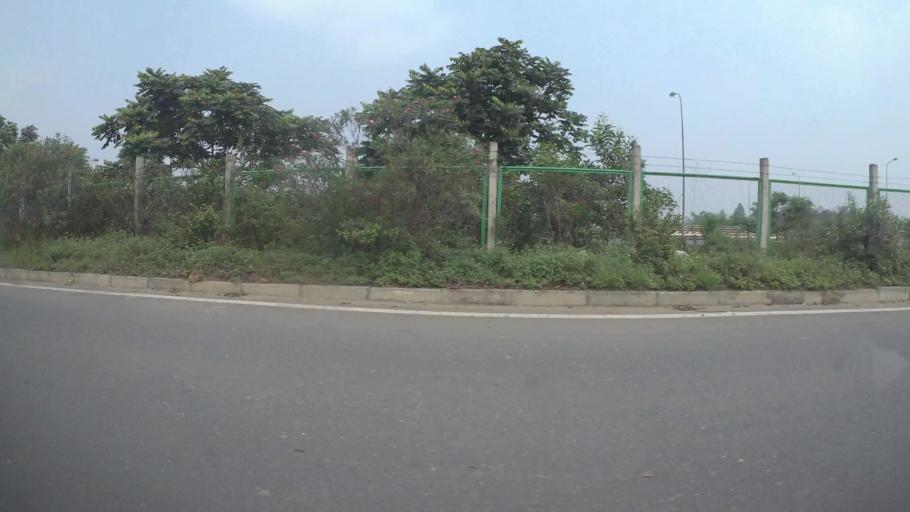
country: VN
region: Ha Noi
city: Quoc Oai
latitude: 20.9951
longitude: 105.5906
